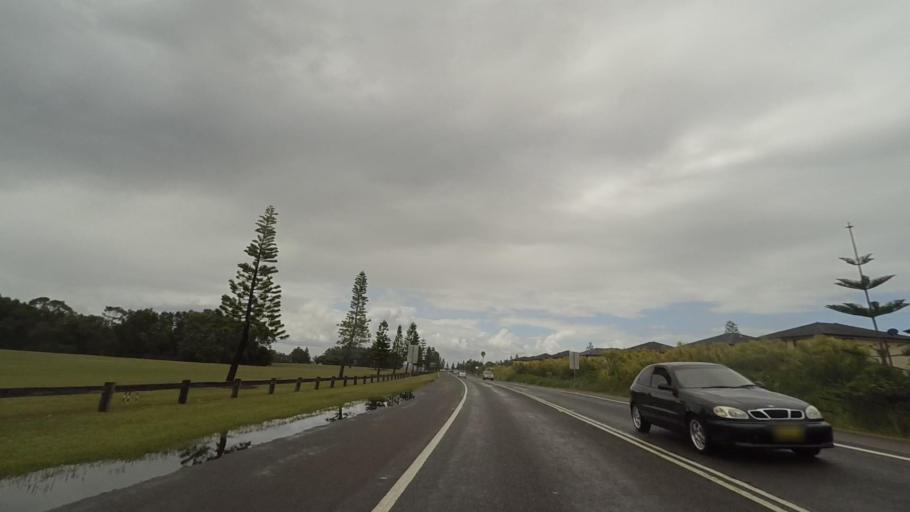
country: AU
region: New South Wales
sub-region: Wyong Shire
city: The Entrance
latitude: -33.3333
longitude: 151.5036
